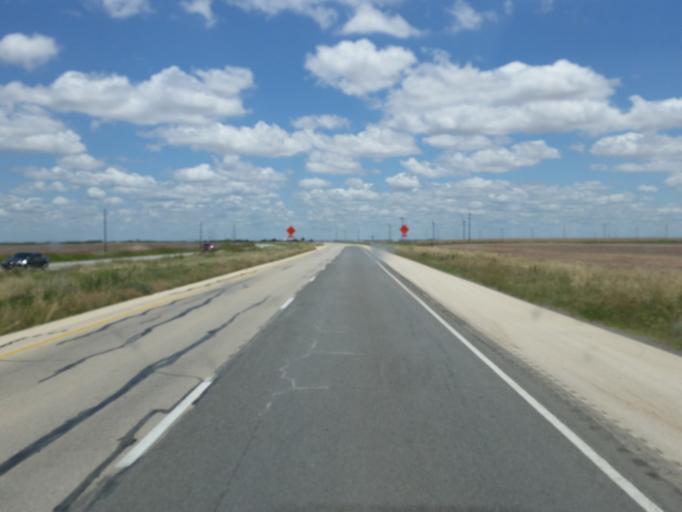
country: US
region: Texas
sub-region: Nolan County
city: Roscoe
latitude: 32.4771
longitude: -100.6138
